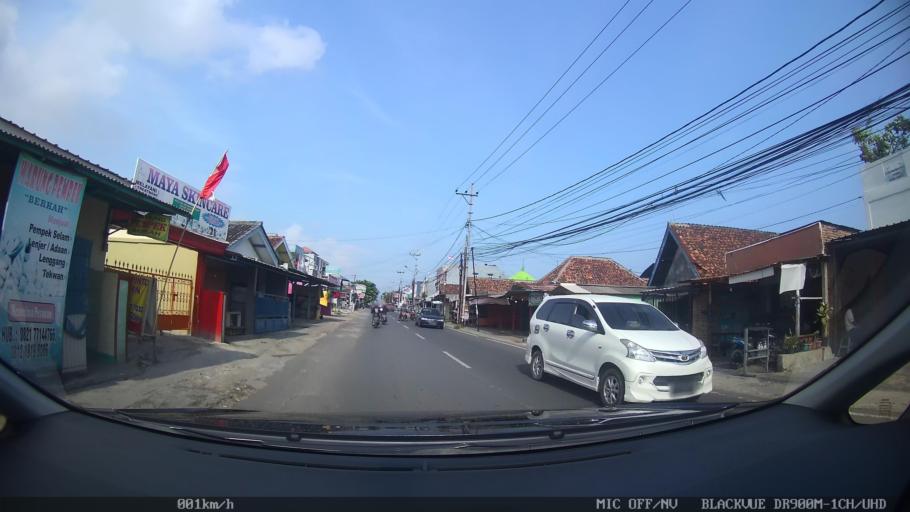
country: ID
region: Lampung
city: Kedaton
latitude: -5.3862
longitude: 105.2662
